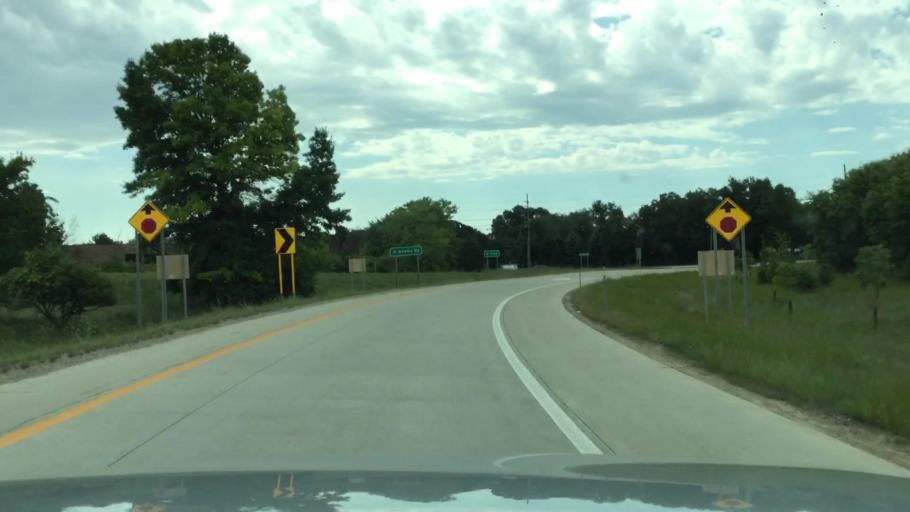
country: US
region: Michigan
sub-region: Oakland County
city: Bloomfield Hills
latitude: 42.6066
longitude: -83.2115
